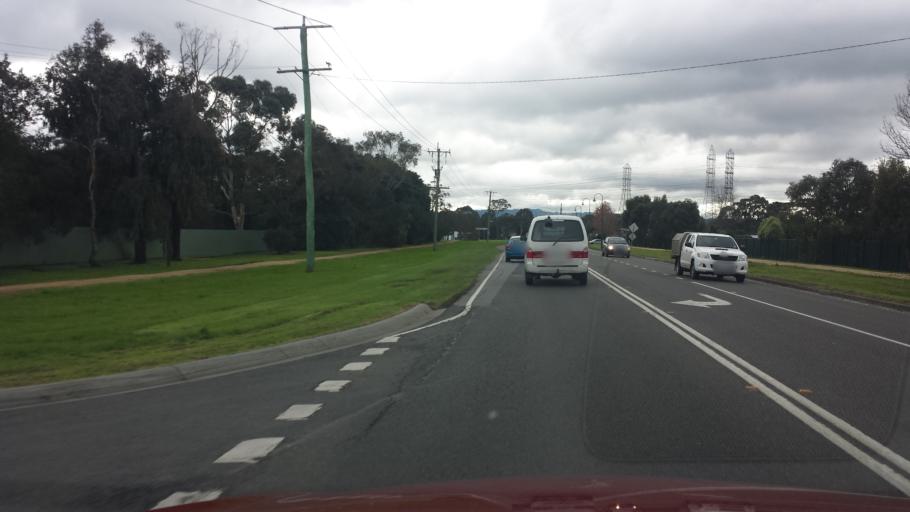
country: AU
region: Victoria
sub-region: Casey
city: Narre Warren North
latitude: -37.9933
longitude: 145.3134
